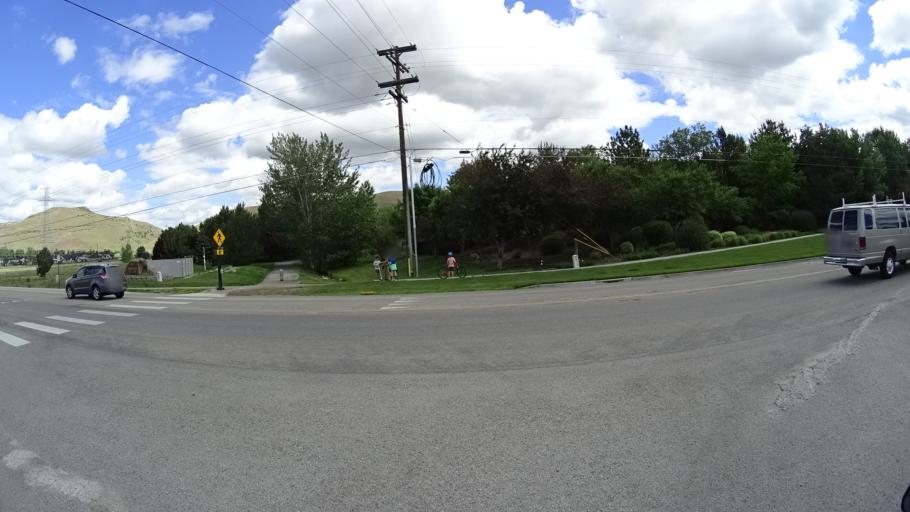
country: US
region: Idaho
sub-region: Ada County
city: Boise
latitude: 43.5706
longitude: -116.1241
